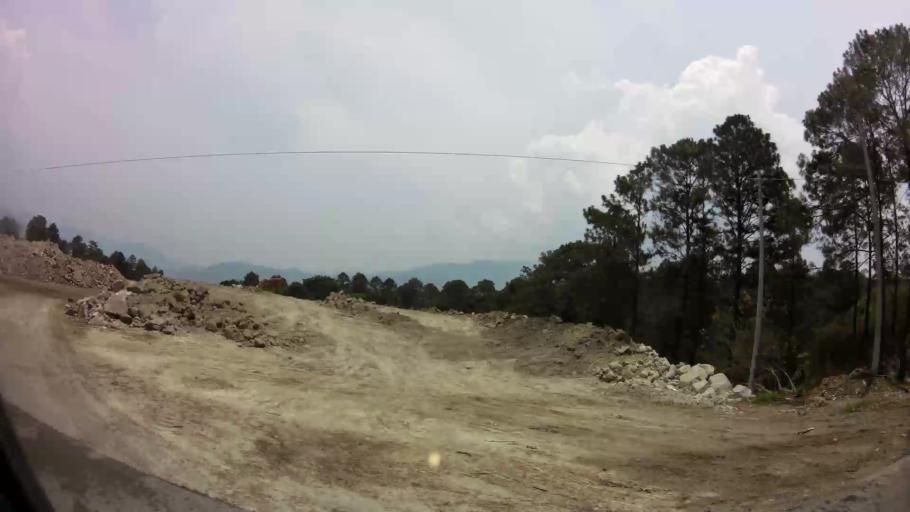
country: HN
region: Comayagua
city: Taulabe
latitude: 14.6747
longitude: -87.9510
